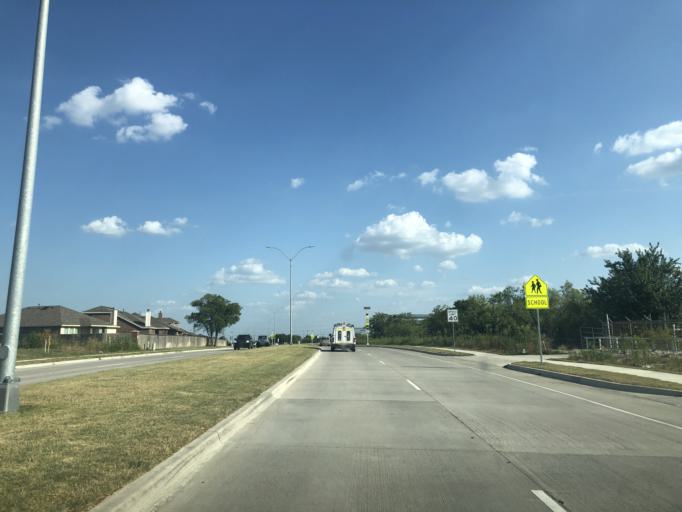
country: US
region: Texas
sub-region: Tarrant County
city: Saginaw
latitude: 32.8454
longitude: -97.3903
